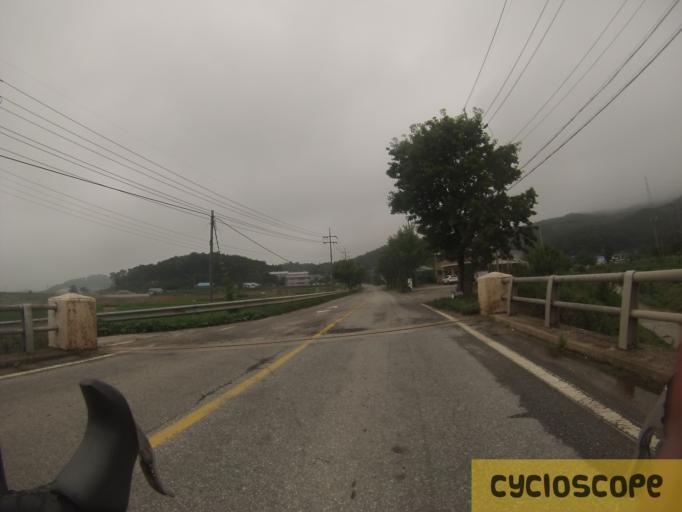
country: KR
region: Chungcheongnam-do
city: Asan
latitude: 36.8606
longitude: 126.9456
